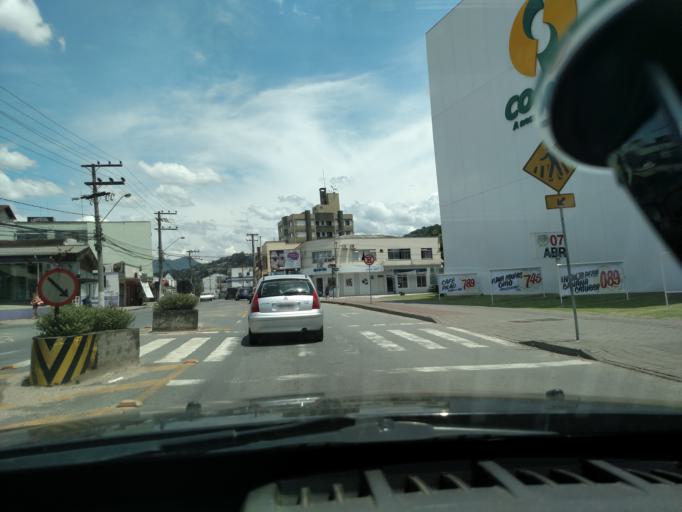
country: BR
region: Santa Catarina
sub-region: Blumenau
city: Blumenau
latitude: -26.9444
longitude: -49.0721
